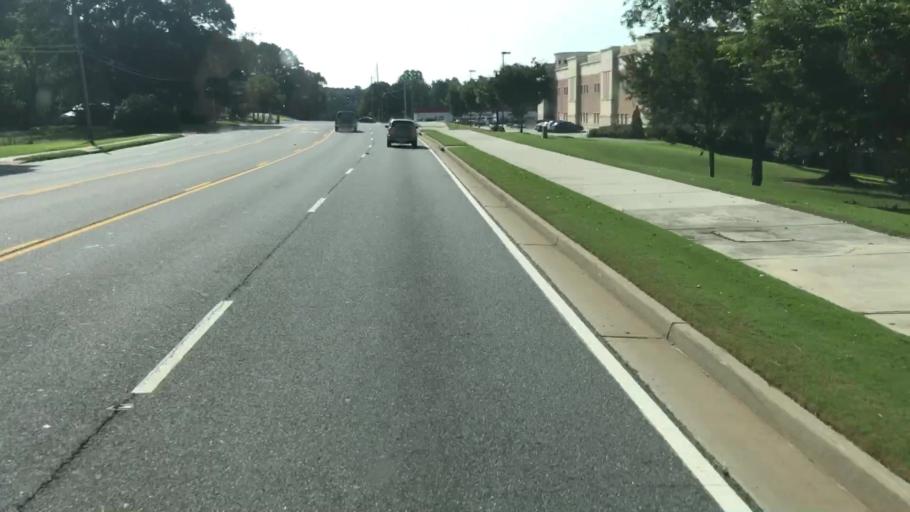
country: US
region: Georgia
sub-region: Gwinnett County
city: Lawrenceville
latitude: 33.9528
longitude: -83.9834
